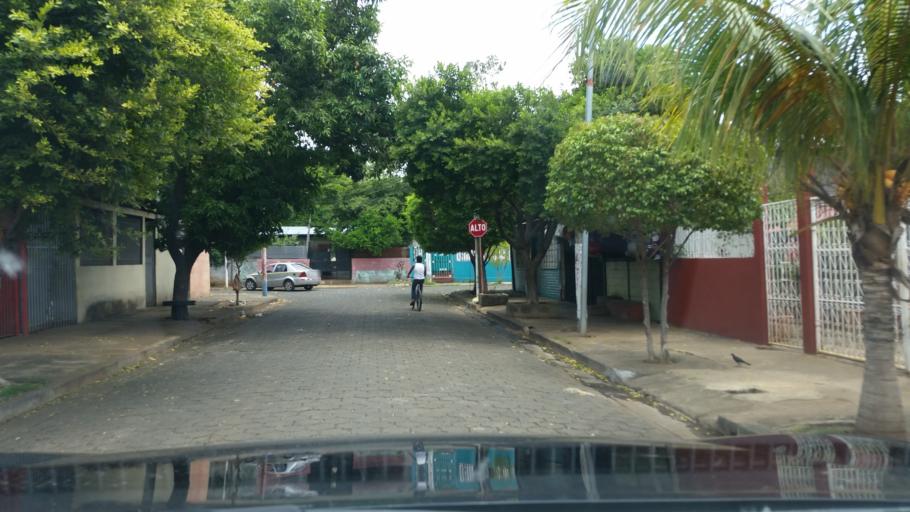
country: NI
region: Managua
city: Managua
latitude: 12.1302
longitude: -86.2603
